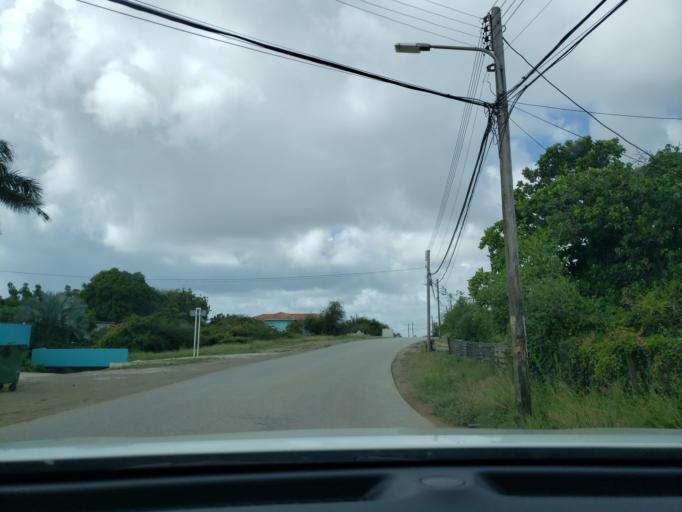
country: CW
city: Willemstad
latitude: 12.0928
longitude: -68.8697
